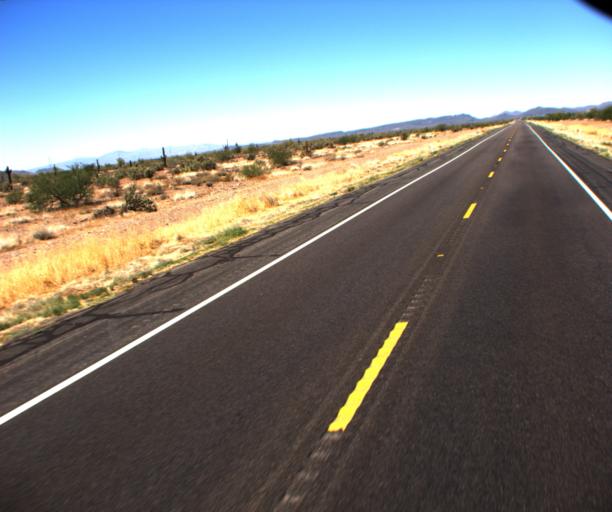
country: US
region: Arizona
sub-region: Maricopa County
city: Anthem
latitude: 33.7978
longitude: -112.1907
